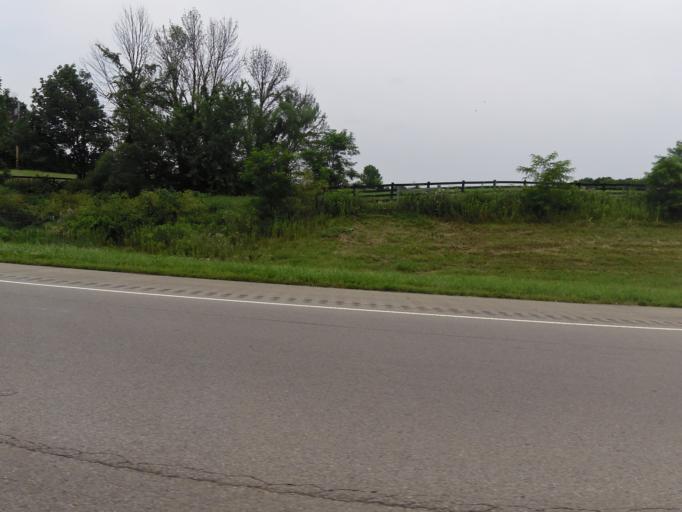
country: US
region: Ohio
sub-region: Clinton County
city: Wilmington
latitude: 39.4635
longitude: -83.8737
